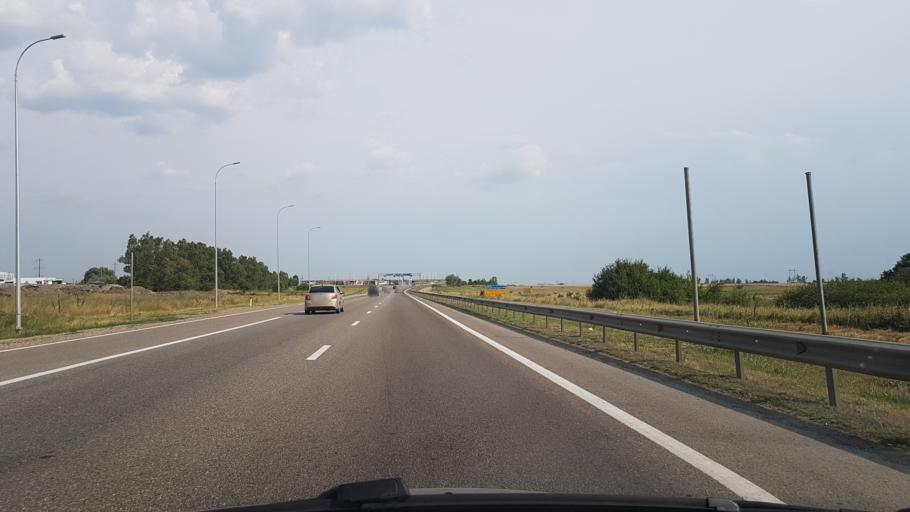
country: RU
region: Adygeya
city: Adygeysk
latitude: 44.9001
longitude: 39.1611
